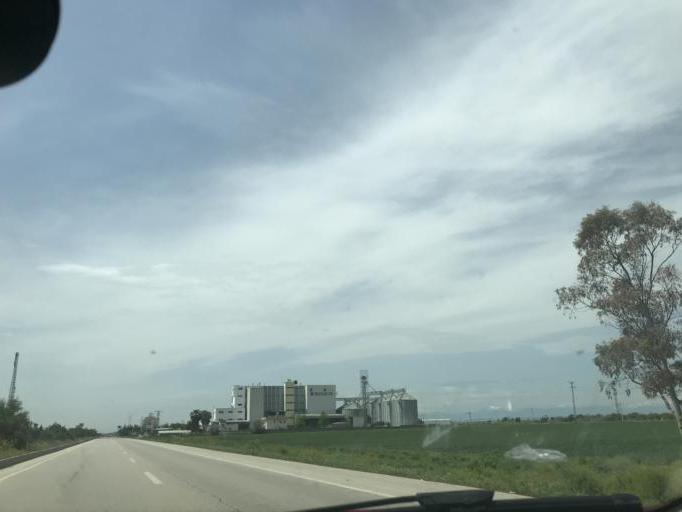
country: TR
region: Adana
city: Yakapinar
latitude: 36.9741
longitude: 35.4996
